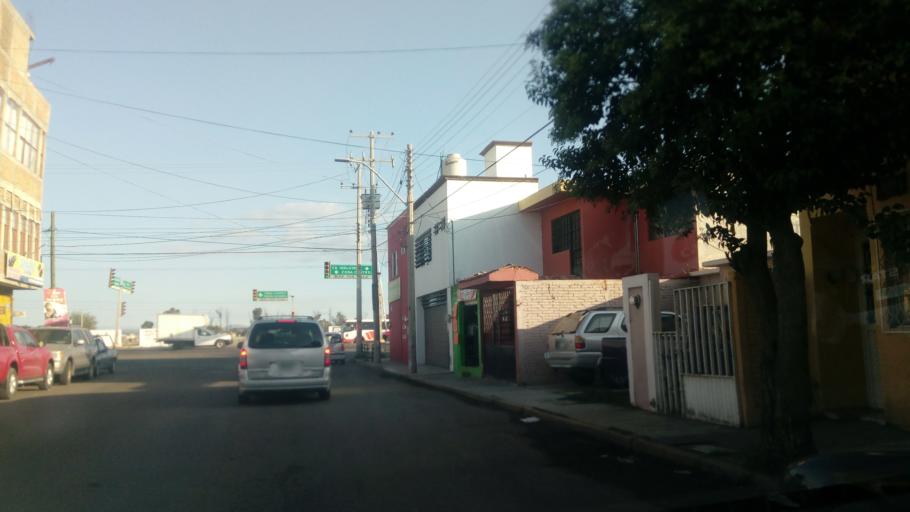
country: MX
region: Durango
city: Victoria de Durango
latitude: 24.0497
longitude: -104.6198
